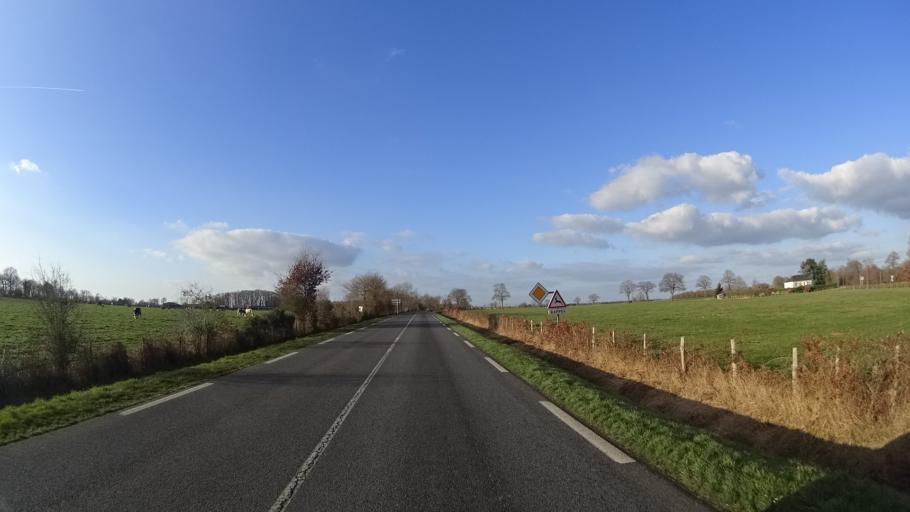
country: FR
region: Pays de la Loire
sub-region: Departement de la Loire-Atlantique
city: Plesse
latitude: 47.5157
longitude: -1.8870
